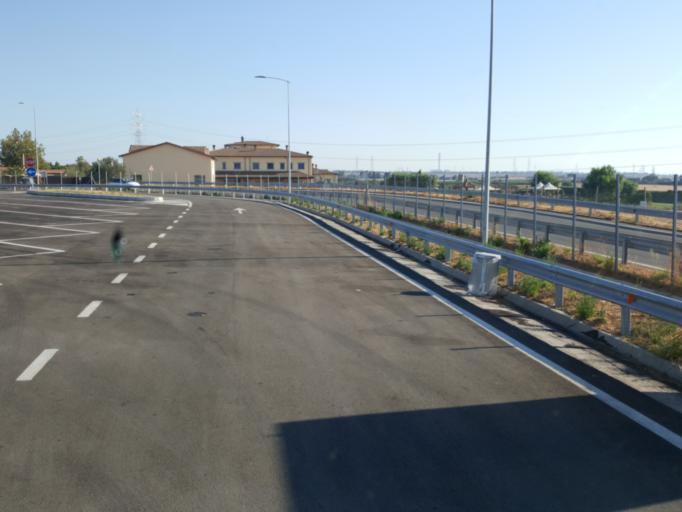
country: IT
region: Latium
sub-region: Citta metropolitana di Roma Capitale
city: Aurelia
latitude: 42.1842
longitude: 11.7880
